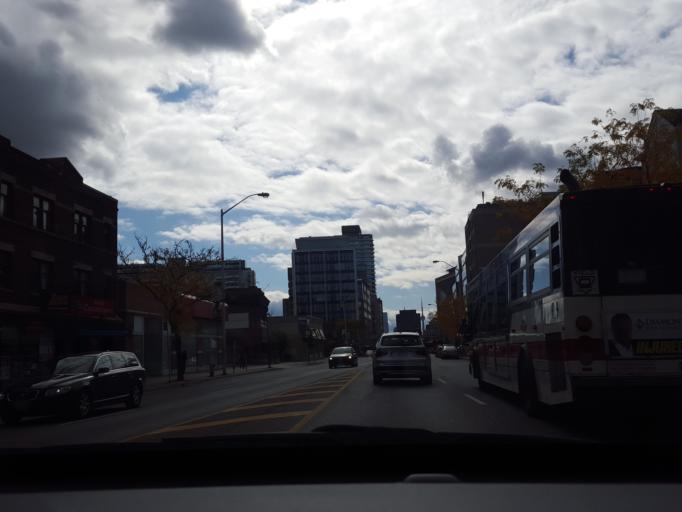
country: CA
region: Ontario
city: Toronto
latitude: 43.7002
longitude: -79.3970
